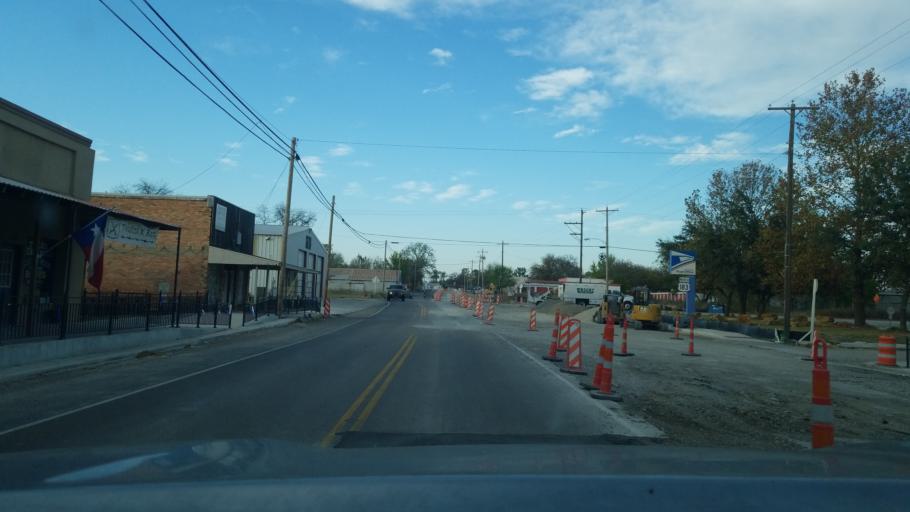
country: US
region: Texas
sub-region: Brown County
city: Lake Brownwood
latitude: 32.0962
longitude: -98.9640
